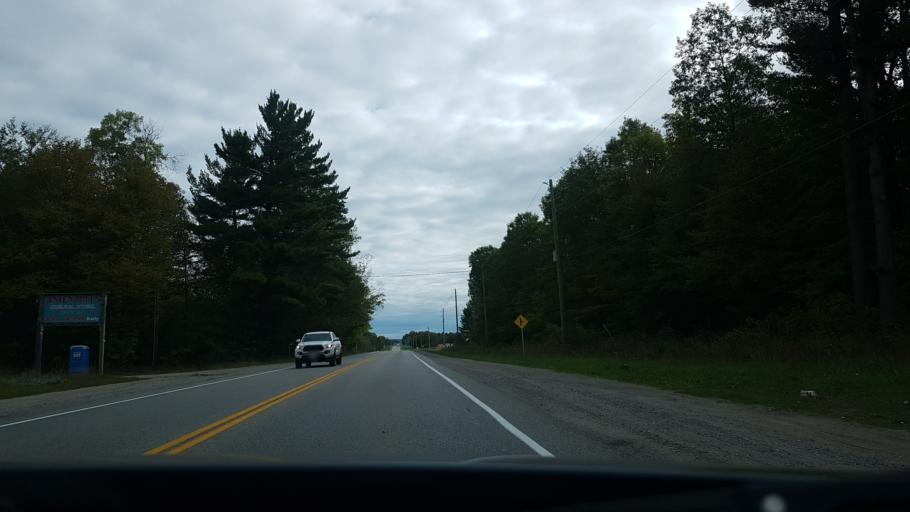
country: CA
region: Ontario
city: Barrie
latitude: 44.4931
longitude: -79.8061
